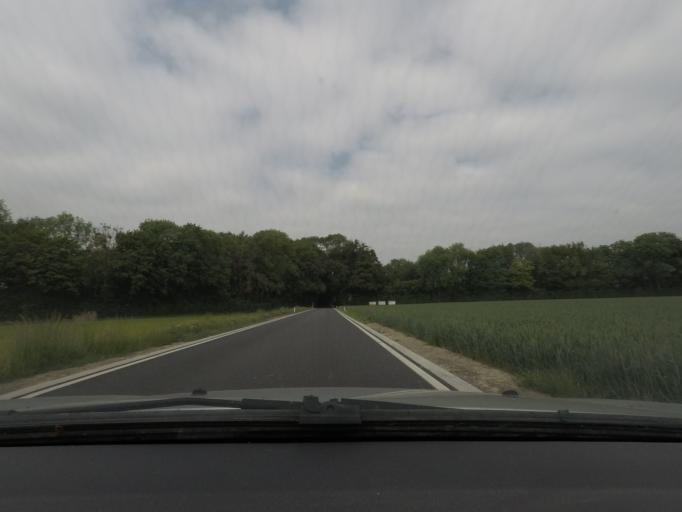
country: BE
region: Wallonia
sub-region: Province de Namur
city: Noville-les-Bois
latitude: 50.4902
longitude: 5.0053
